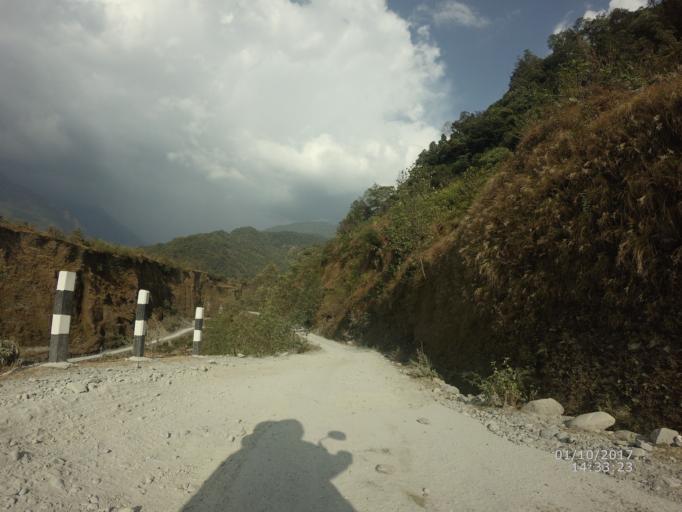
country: NP
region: Western Region
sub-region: Gandaki Zone
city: Pokhara
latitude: 28.3389
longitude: 83.9634
